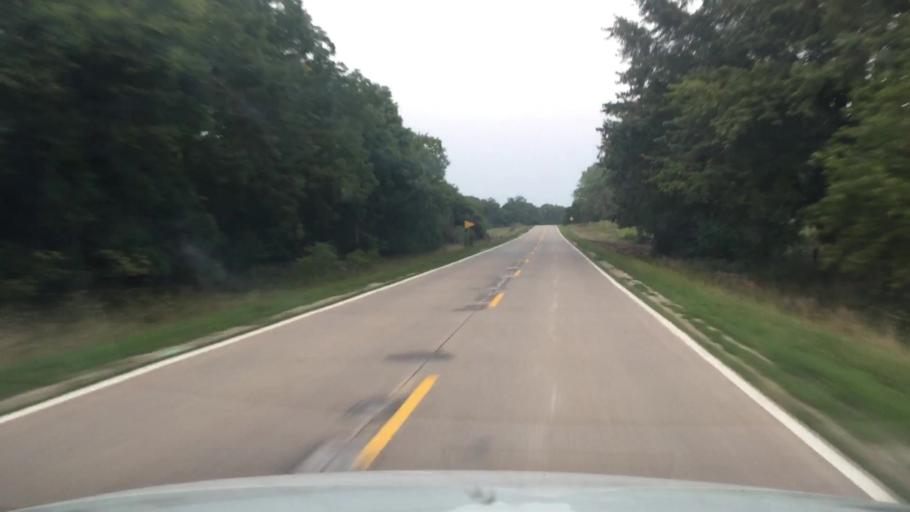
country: US
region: Iowa
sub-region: Warren County
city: Indianola
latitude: 41.1908
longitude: -93.6414
